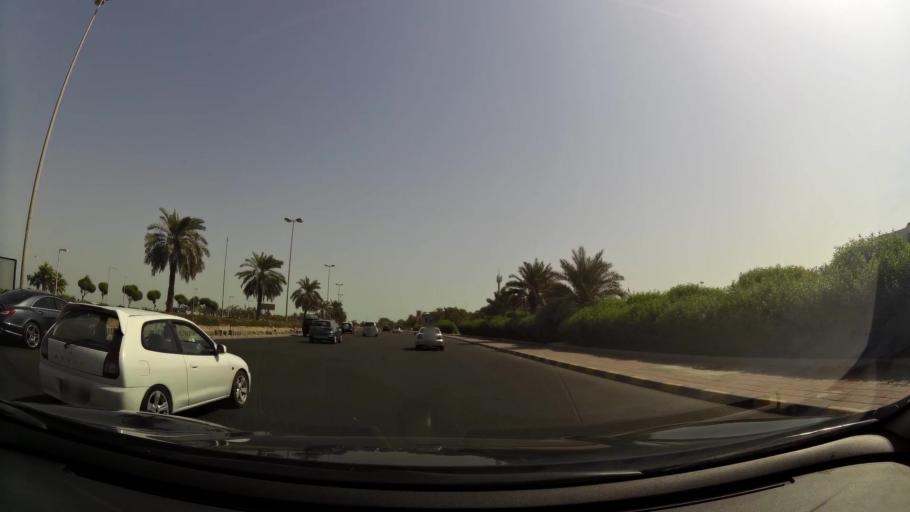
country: KW
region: Al Asimah
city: Ad Dasmah
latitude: 29.3683
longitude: 48.0138
